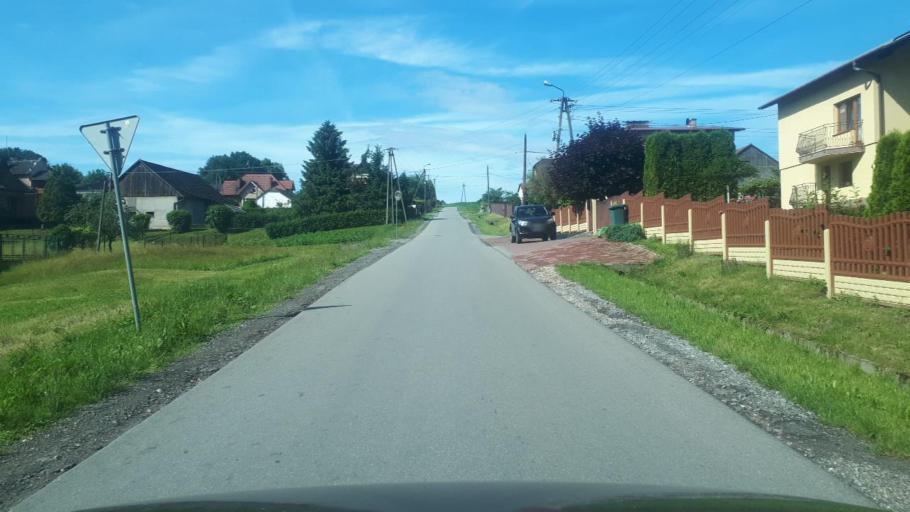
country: PL
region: Silesian Voivodeship
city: Janowice
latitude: 49.9054
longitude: 19.1157
